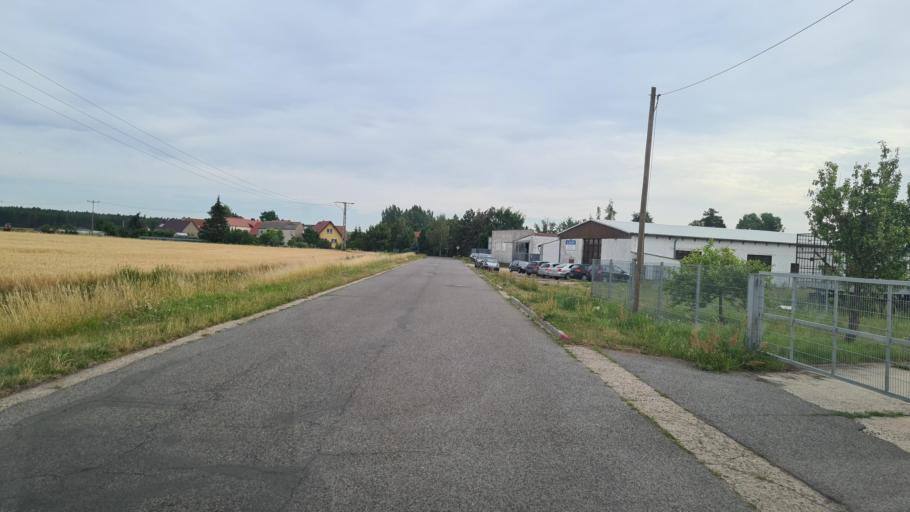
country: DE
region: Saxony-Anhalt
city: Jessen
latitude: 51.7741
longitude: 12.9291
